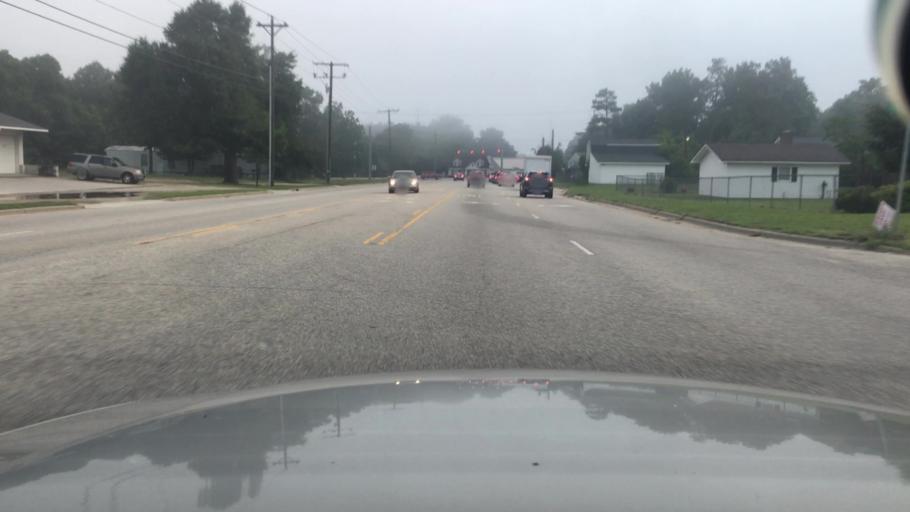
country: US
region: North Carolina
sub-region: Cumberland County
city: Hope Mills
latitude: 35.0164
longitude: -78.9187
